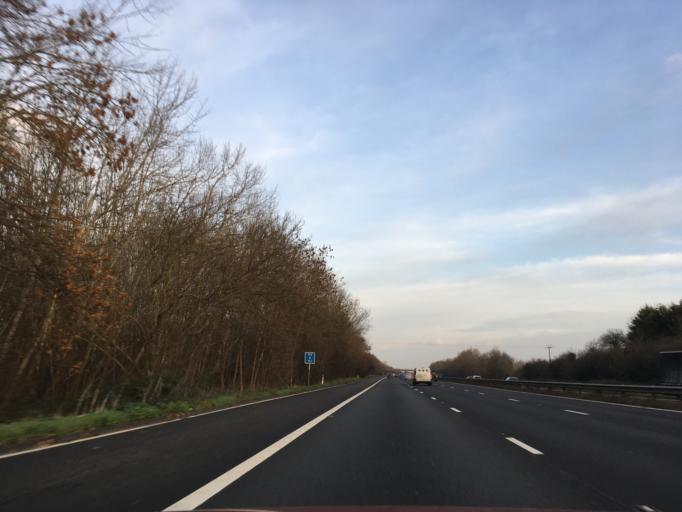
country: GB
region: England
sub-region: Gloucestershire
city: Uckington
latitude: 51.9514
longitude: -2.1267
